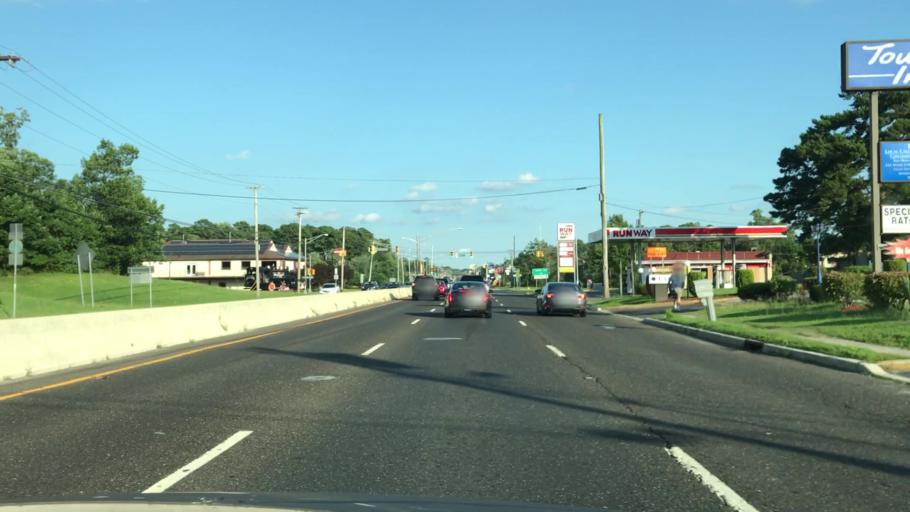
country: US
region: New Jersey
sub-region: Atlantic County
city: Absecon
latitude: 39.4497
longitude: -74.5339
